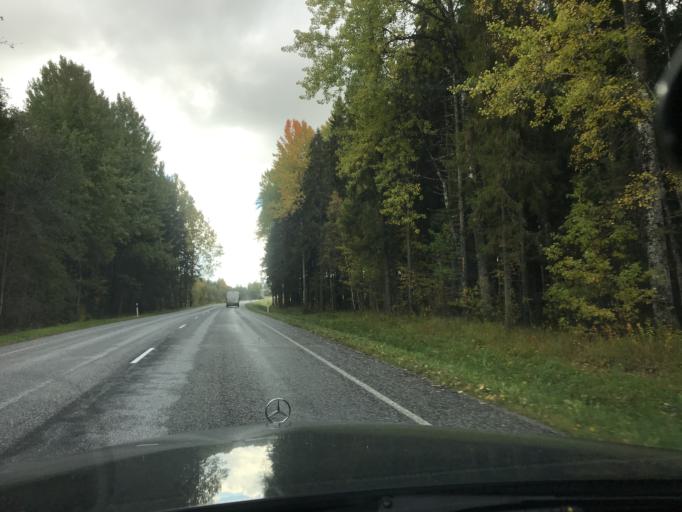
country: RU
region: Pskov
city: Pechory
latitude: 57.7216
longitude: 27.3160
